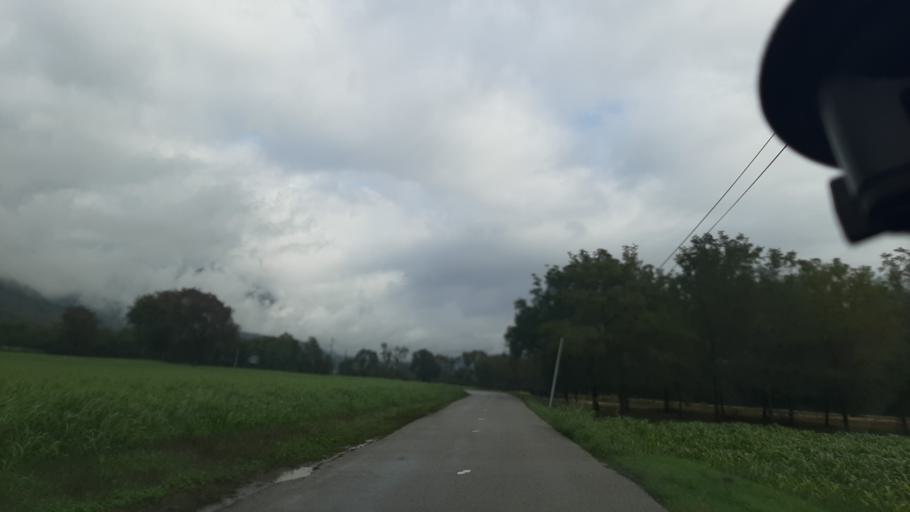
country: FR
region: Rhone-Alpes
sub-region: Departement de la Savoie
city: Frontenex
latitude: 45.6173
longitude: 6.2883
